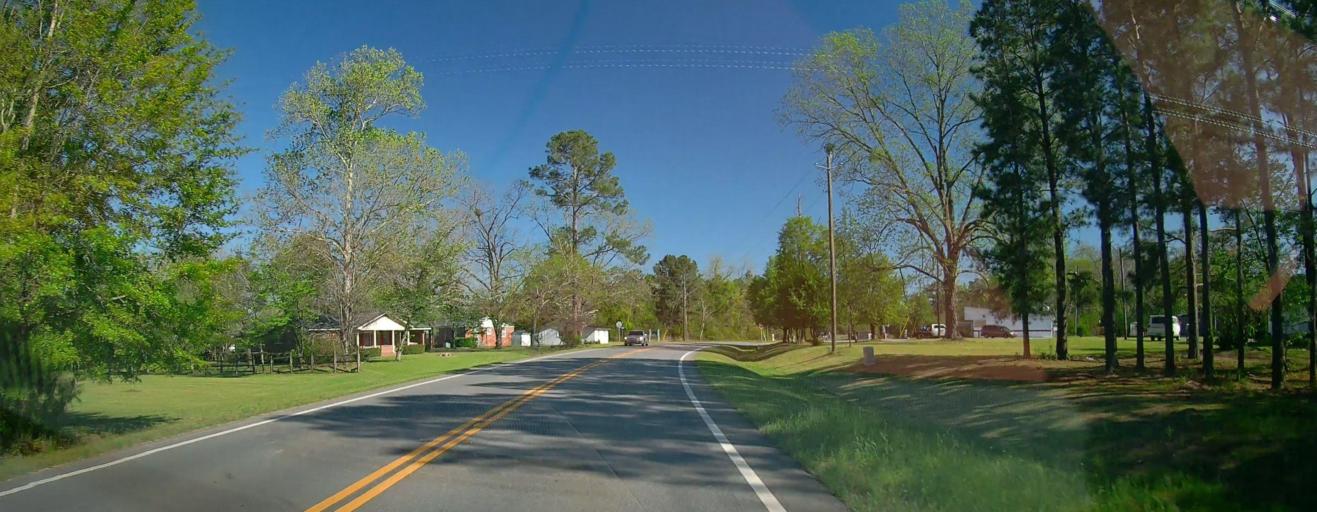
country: US
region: Georgia
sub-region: Pulaski County
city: Hawkinsville
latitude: 32.1304
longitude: -83.5017
